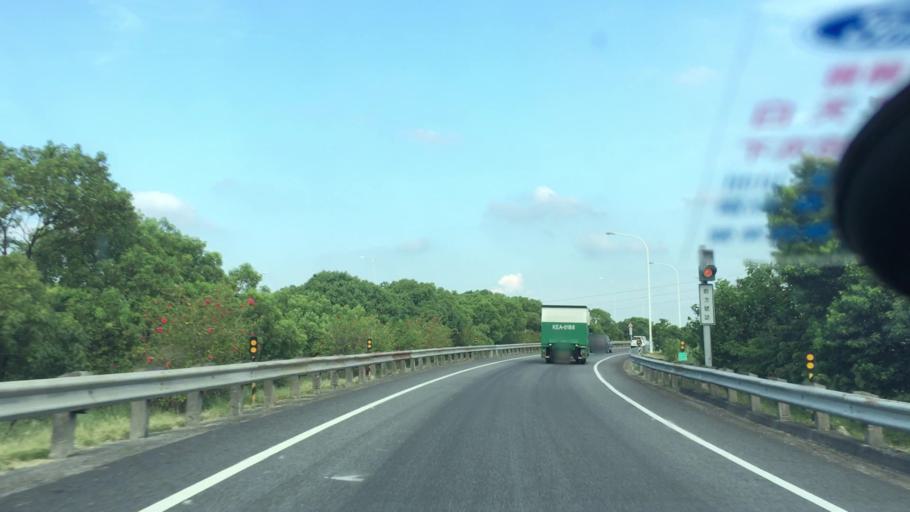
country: TW
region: Taiwan
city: Taoyuan City
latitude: 25.0164
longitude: 121.2737
